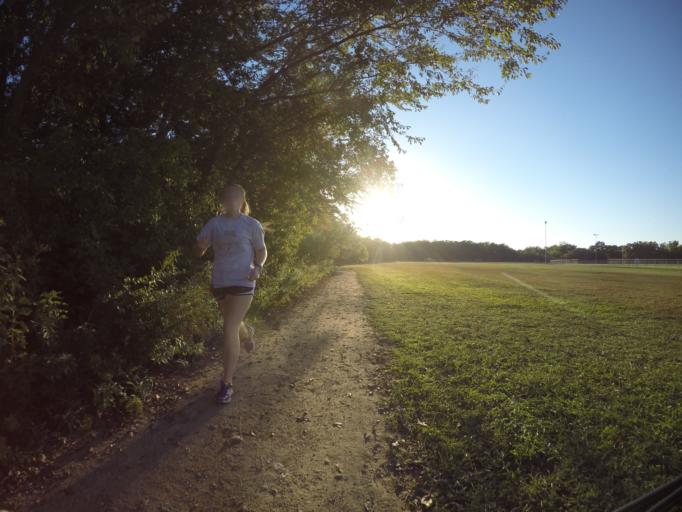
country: US
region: Kansas
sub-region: Riley County
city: Manhattan
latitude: 39.1824
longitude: -96.6316
